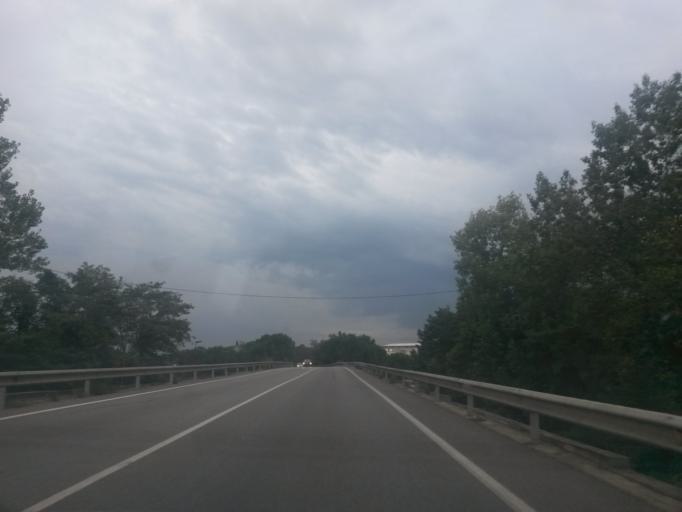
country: ES
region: Catalonia
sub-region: Provincia de Girona
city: Cornella del Terri
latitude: 42.0990
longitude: 2.7975
